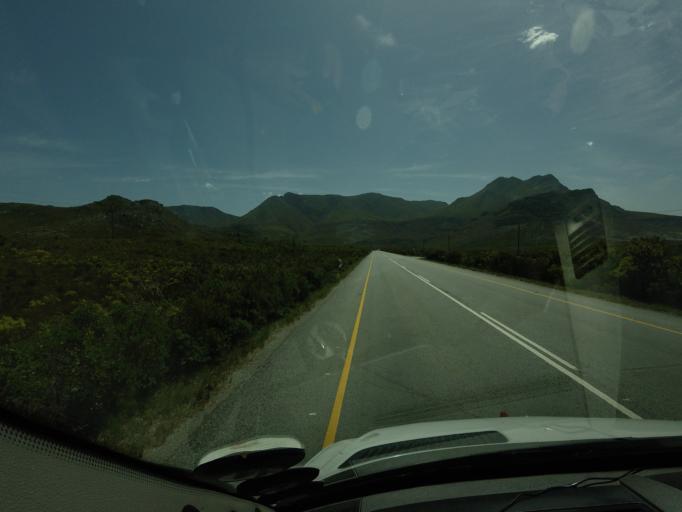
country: ZA
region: Western Cape
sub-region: Overberg District Municipality
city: Grabouw
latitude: -34.3413
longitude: 18.9834
